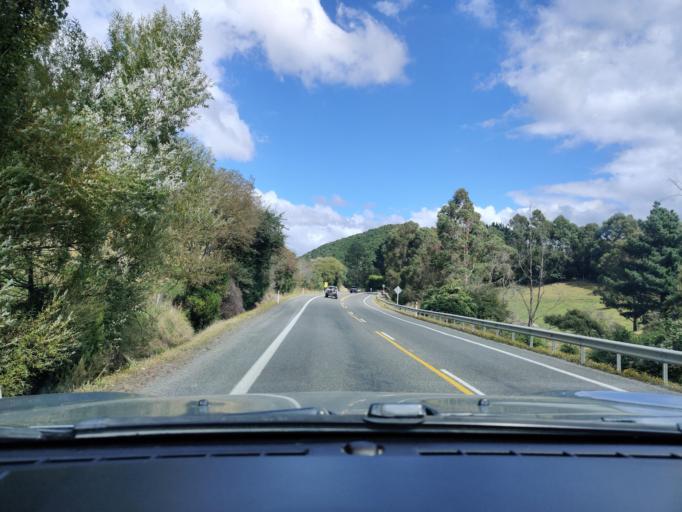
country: NZ
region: Marlborough
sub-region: Marlborough District
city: Picton
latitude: -41.3097
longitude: 173.9815
